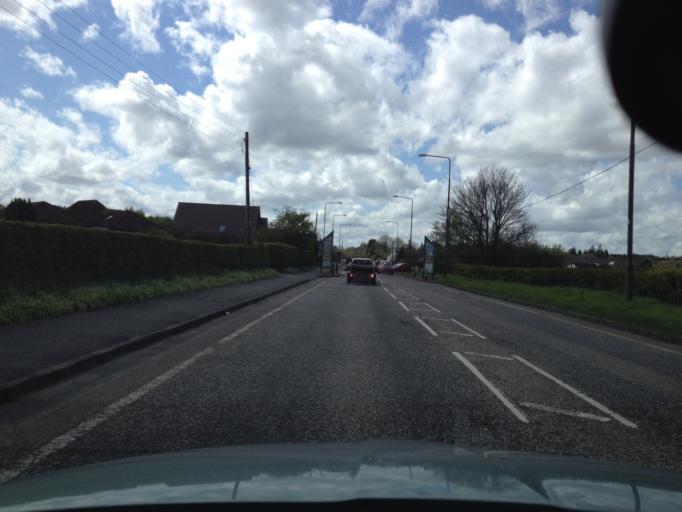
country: GB
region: Scotland
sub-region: West Lothian
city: Livingston
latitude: 55.9226
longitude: -3.5319
